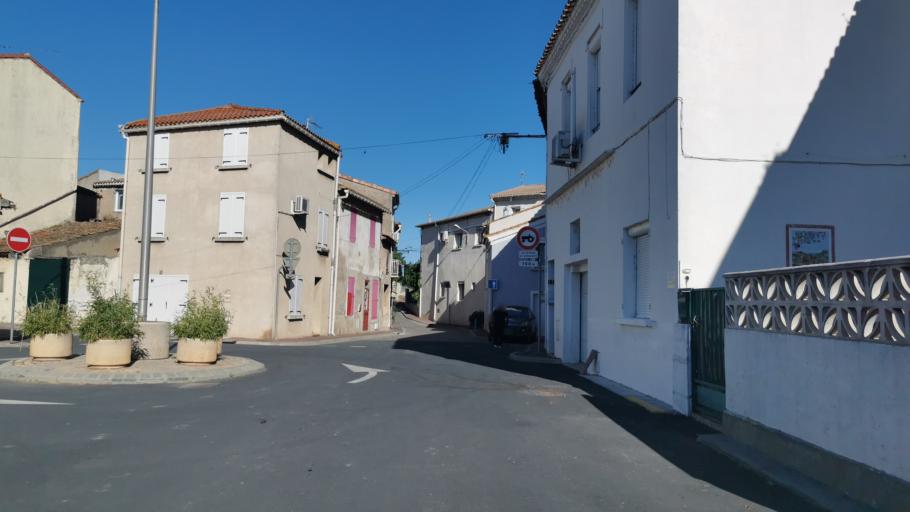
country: FR
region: Languedoc-Roussillon
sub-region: Departement de l'Aude
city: Coursan
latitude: 43.2367
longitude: 3.0613
